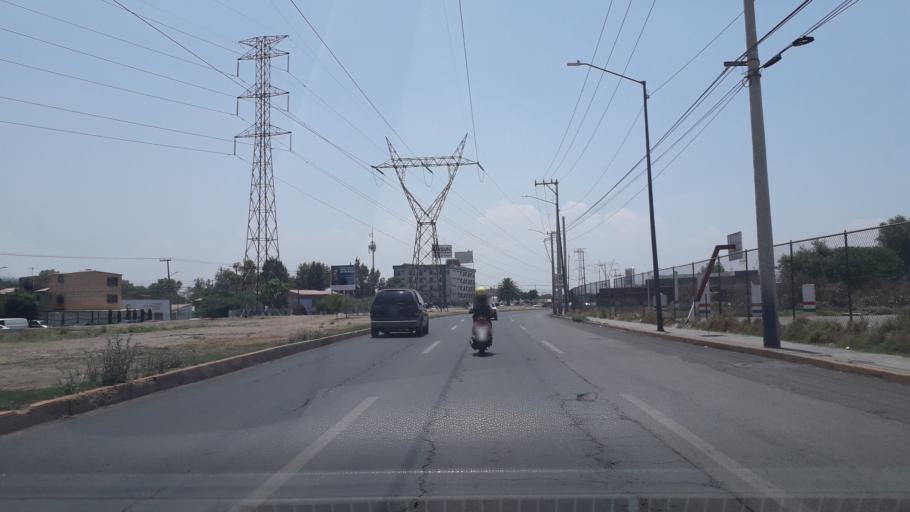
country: MX
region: Mexico
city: Coacalco
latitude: 19.6426
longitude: -99.1123
